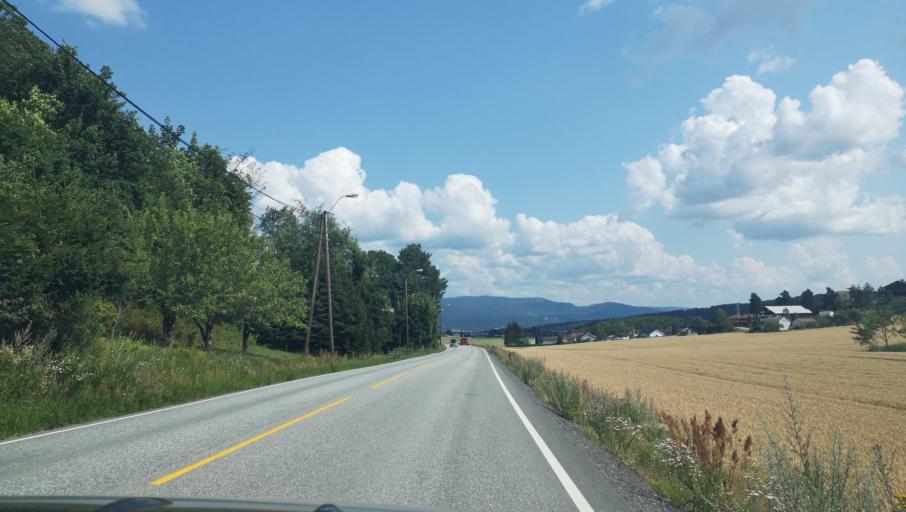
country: NO
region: Buskerud
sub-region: Ovre Eiker
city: Hokksund
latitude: 59.7362
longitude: 9.8518
